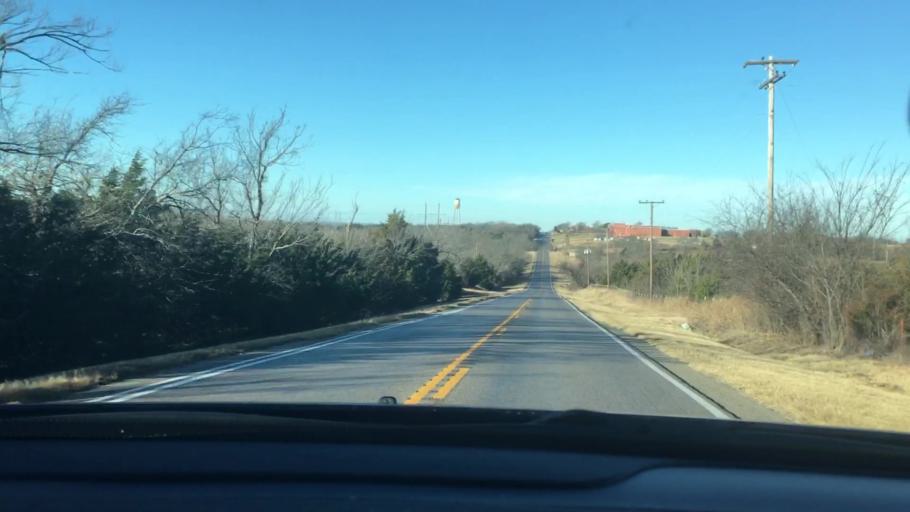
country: US
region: Oklahoma
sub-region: Murray County
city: Sulphur
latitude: 34.5109
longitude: -96.9407
